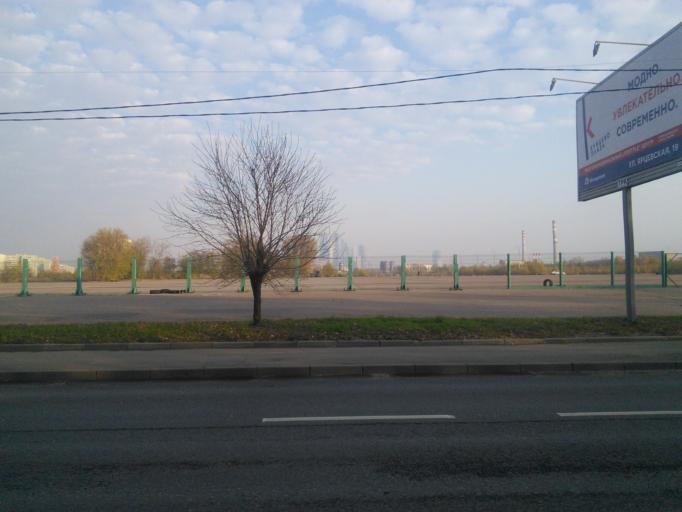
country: RU
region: Moskovskaya
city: Fili
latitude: 55.7623
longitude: 37.4670
